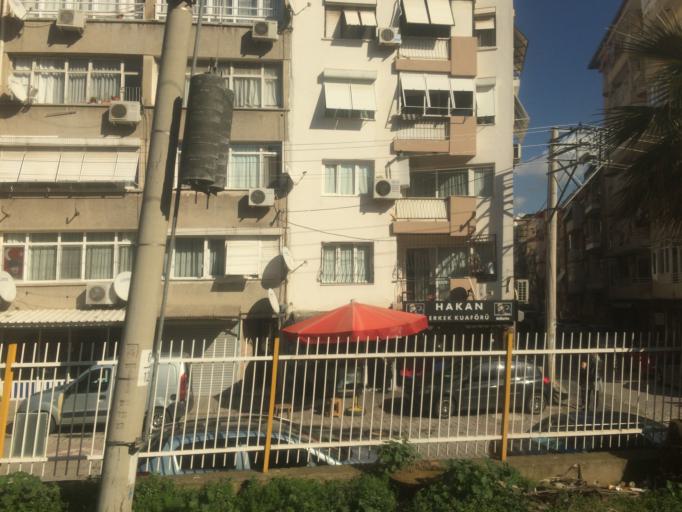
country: TR
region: Izmir
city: Karsiyaka
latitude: 38.4668
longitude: 27.1617
